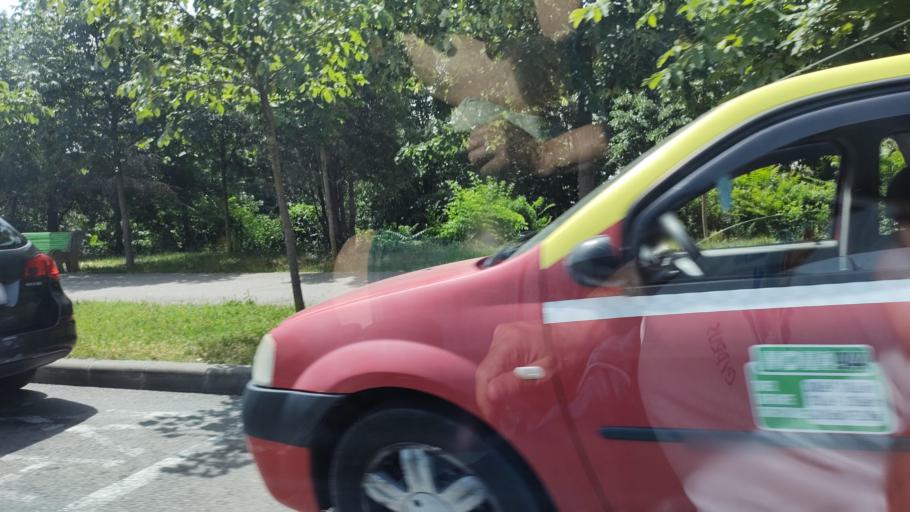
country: RO
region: Mehedinti
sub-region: Municipiul Drobeta-Turnu Severin
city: Drobeta-Turnu Severin
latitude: 44.6231
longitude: 22.6434
